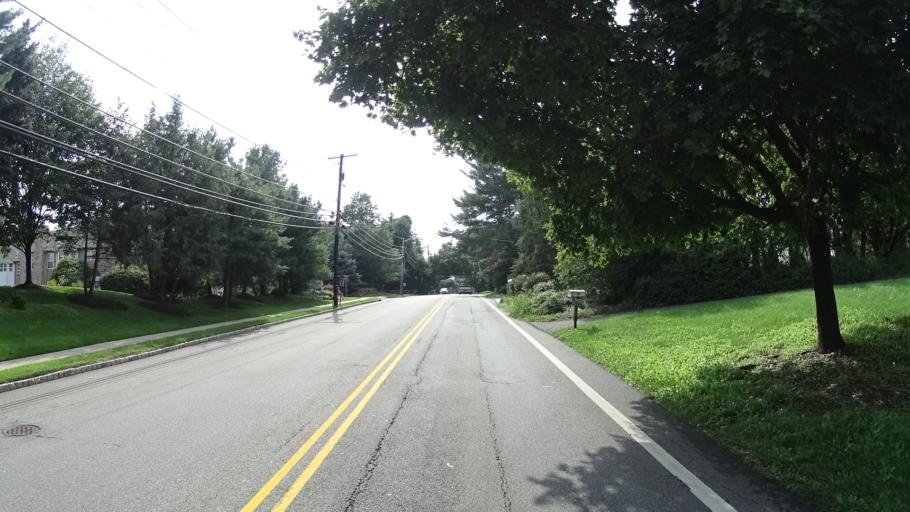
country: US
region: New Jersey
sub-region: Somerset County
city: Watchung
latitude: 40.6673
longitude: -74.5006
